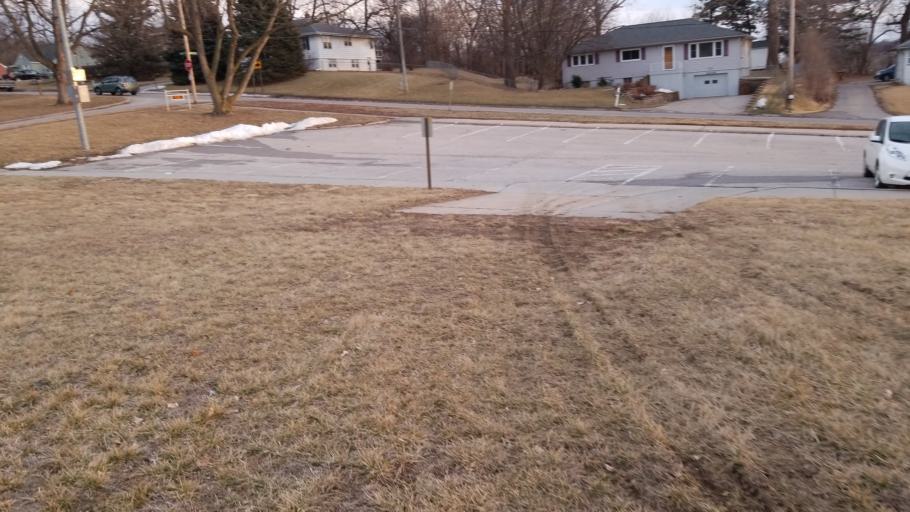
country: US
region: Nebraska
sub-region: Sarpy County
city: Bellevue
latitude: 41.1856
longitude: -95.9304
